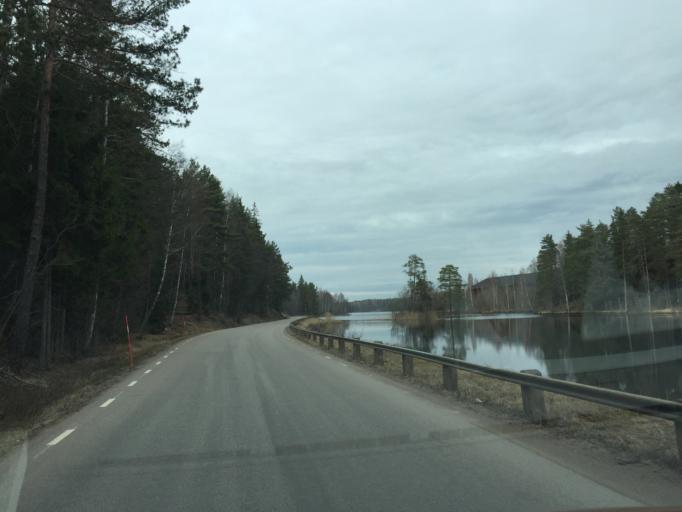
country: SE
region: OEstergoetland
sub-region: Finspangs Kommun
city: Finspang
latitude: 58.7506
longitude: 15.8277
